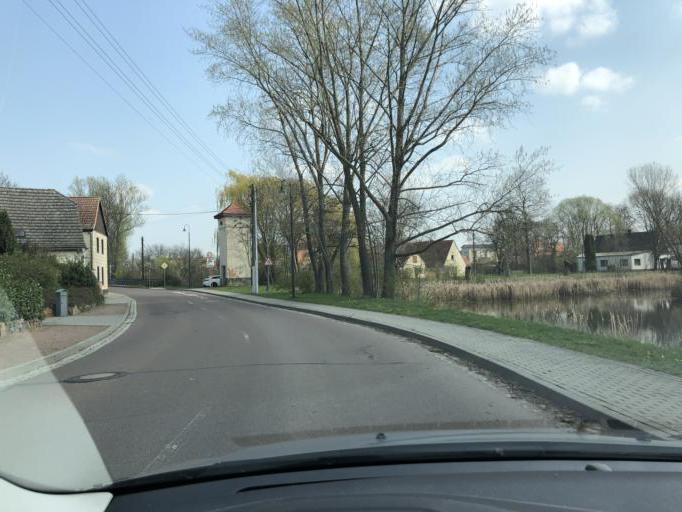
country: DE
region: Saxony-Anhalt
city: Niemberg
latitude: 51.5641
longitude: 12.1312
